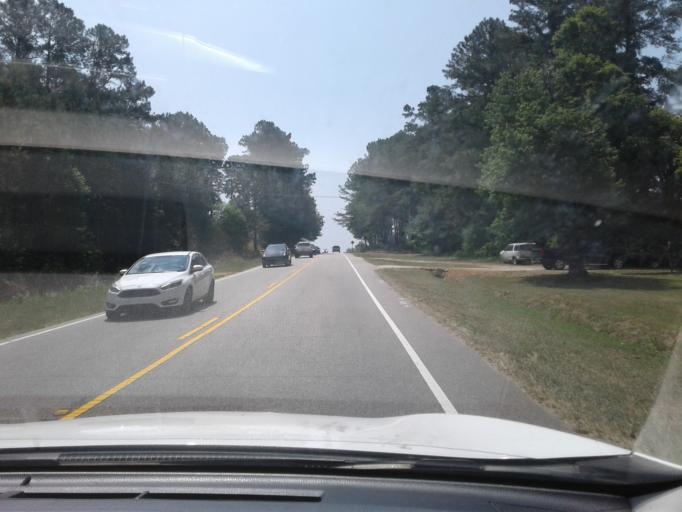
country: US
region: North Carolina
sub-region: Harnett County
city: Coats
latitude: 35.4277
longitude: -78.6776
